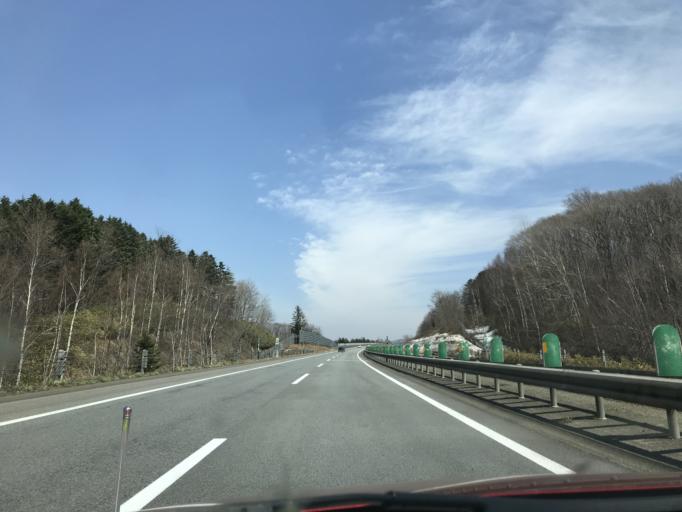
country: JP
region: Hokkaido
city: Bibai
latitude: 43.2594
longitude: 141.8353
